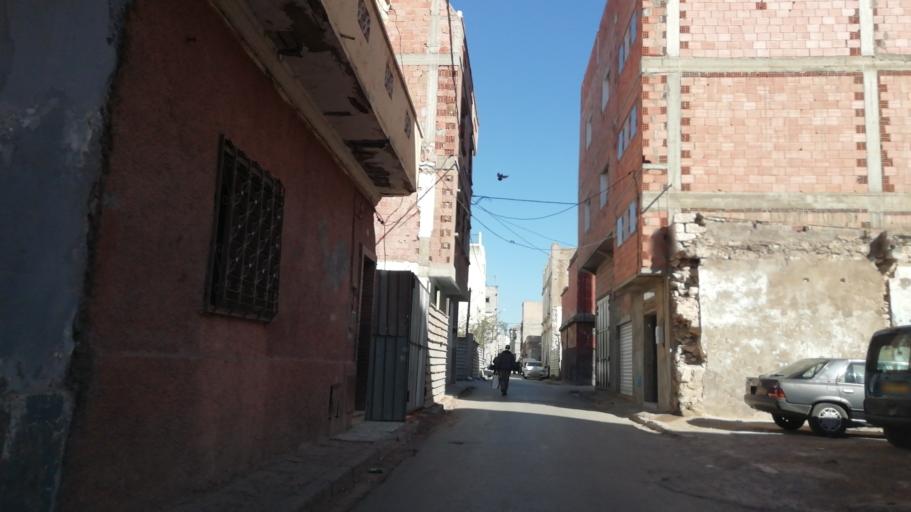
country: DZ
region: Oran
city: Oran
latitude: 35.6874
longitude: -0.6385
